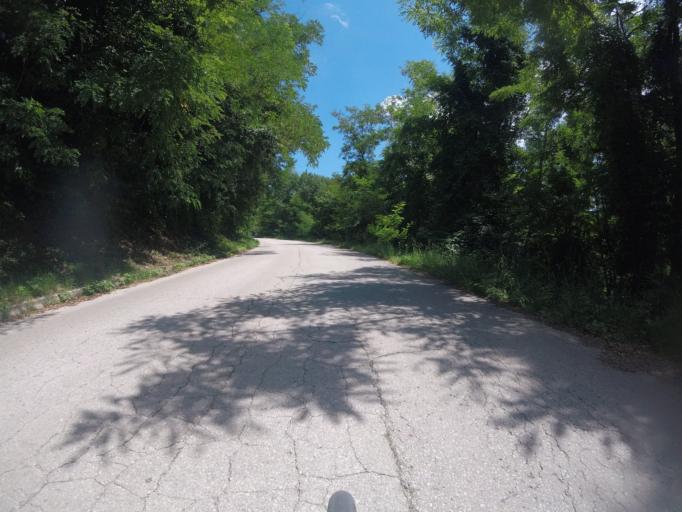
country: HR
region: Karlovacka
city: Ozalj
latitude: 45.6681
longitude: 15.4251
